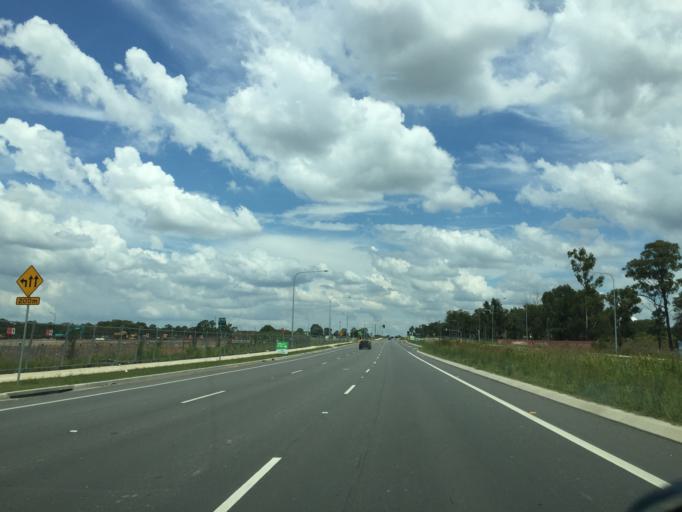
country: AU
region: New South Wales
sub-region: Blacktown
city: Hassall Grove
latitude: -33.7214
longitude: 150.8443
